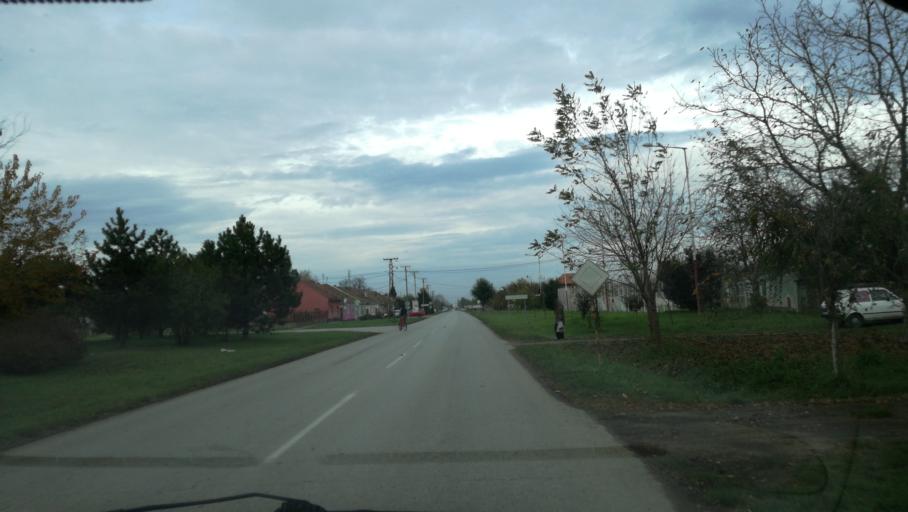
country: RS
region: Autonomna Pokrajina Vojvodina
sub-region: Severnobanatski Okrug
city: Kikinda
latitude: 45.8390
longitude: 20.4548
